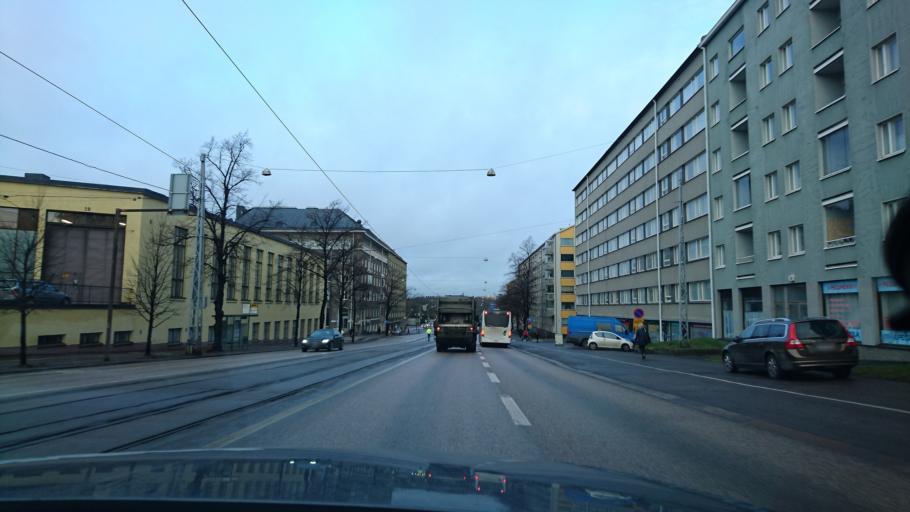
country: FI
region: Uusimaa
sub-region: Helsinki
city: Helsinki
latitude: 60.1951
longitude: 24.9633
